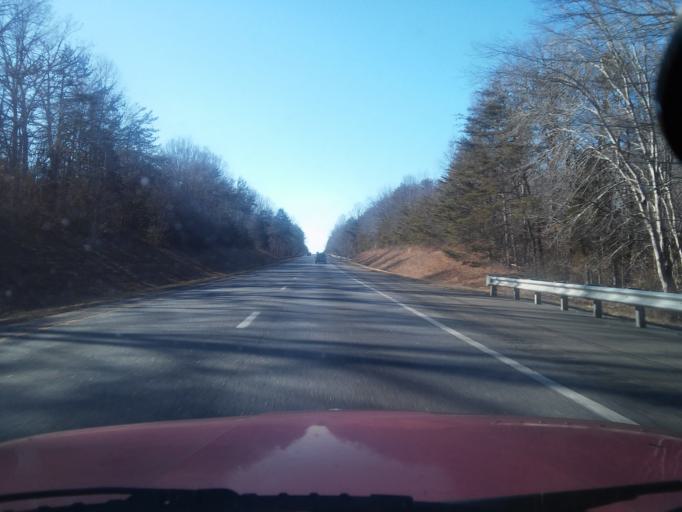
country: US
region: Virginia
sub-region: Fluvanna County
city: Lake Monticello
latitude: 37.9946
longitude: -78.2593
